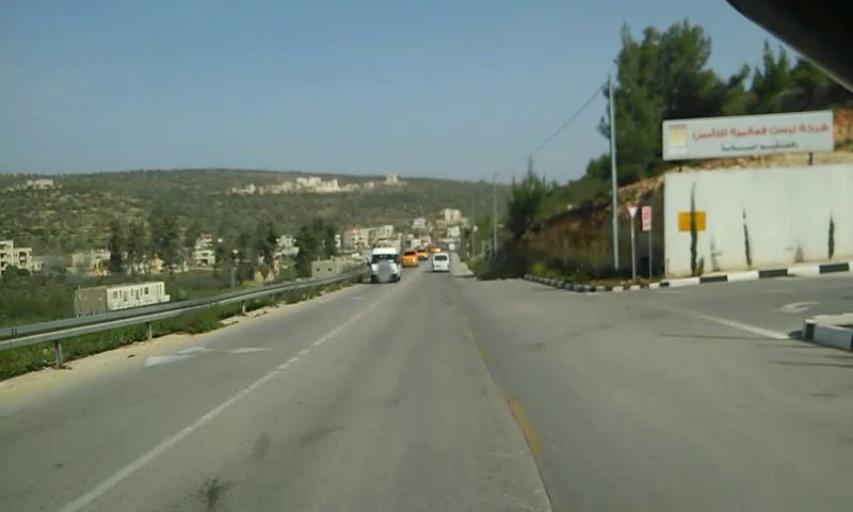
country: PS
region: West Bank
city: Dura al Qar`
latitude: 31.9662
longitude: 35.2279
